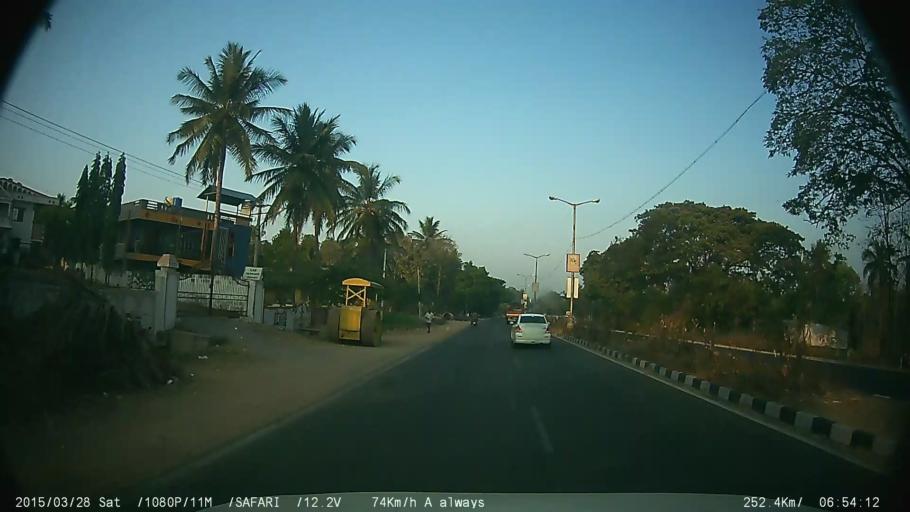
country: IN
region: Karnataka
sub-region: Mandya
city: Maddur
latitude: 12.5803
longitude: 77.0303
